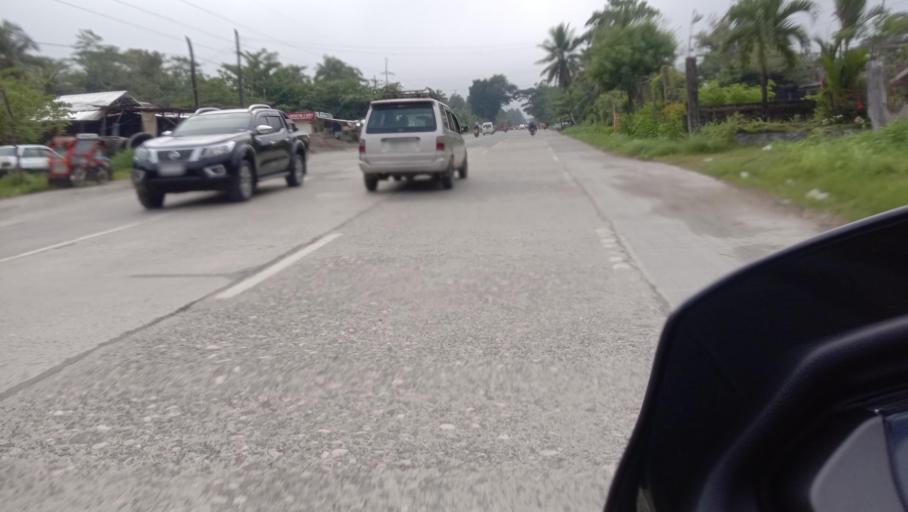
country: PH
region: Caraga
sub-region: Province of Agusan del Sur
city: Alegria
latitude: 8.5053
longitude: 125.9898
